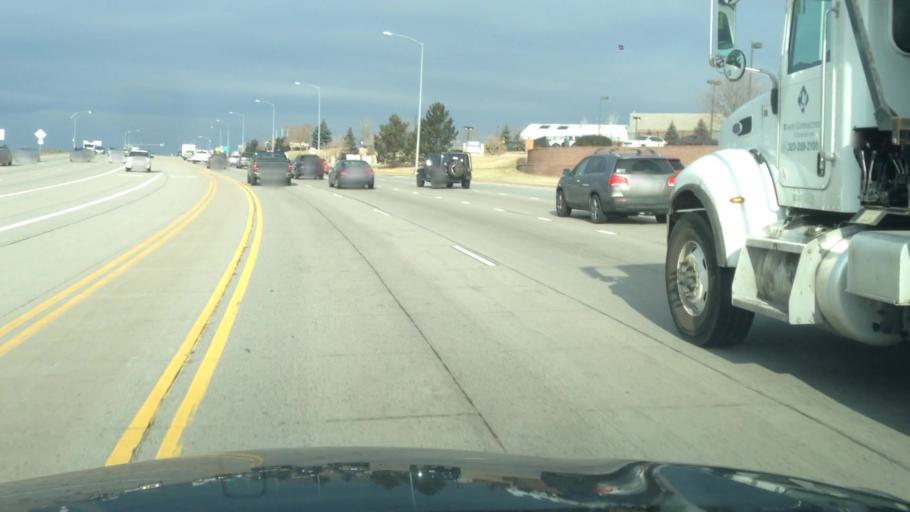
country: US
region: Colorado
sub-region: Arapahoe County
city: Dove Valley
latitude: 39.6111
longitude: -104.8111
